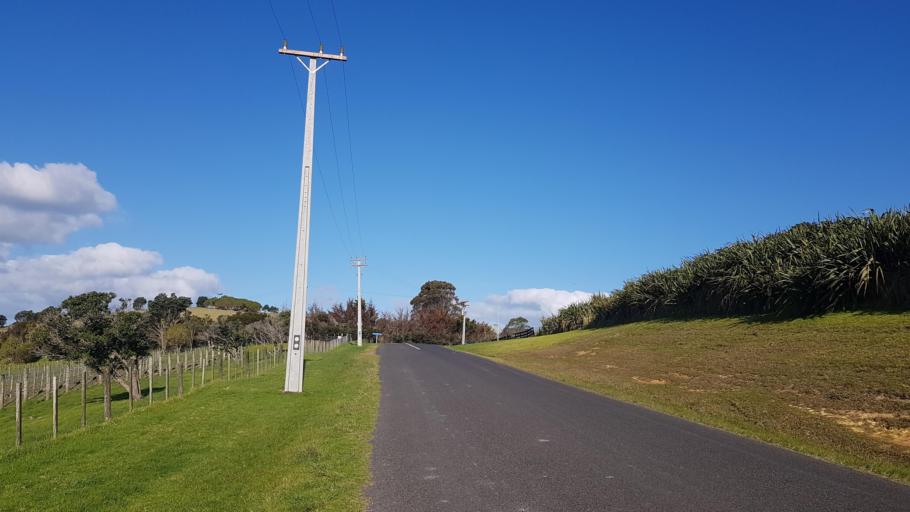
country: NZ
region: Auckland
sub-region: Auckland
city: Pakuranga
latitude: -36.7868
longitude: 175.0003
